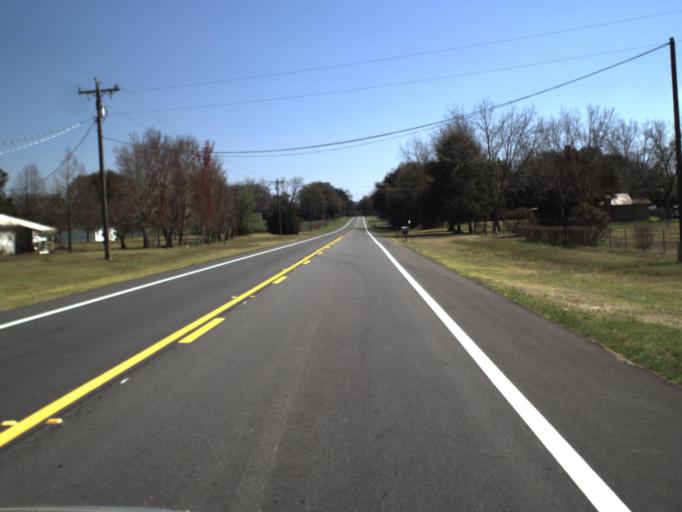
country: US
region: Florida
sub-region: Jackson County
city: Malone
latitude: 30.8573
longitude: -85.0929
